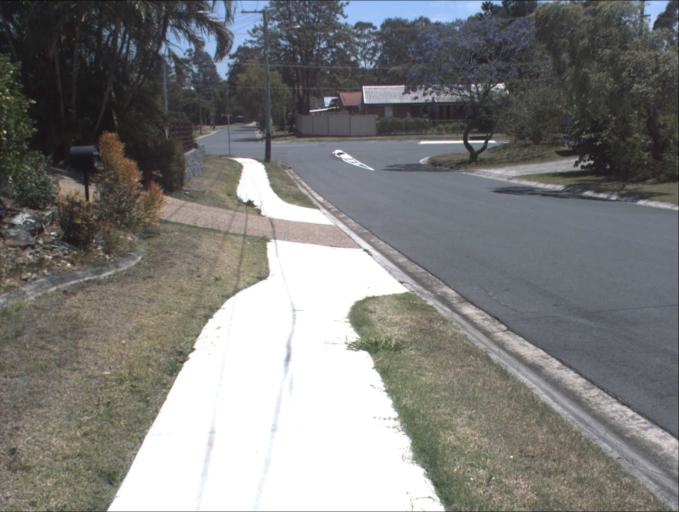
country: AU
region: Queensland
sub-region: Logan
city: Slacks Creek
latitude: -27.6359
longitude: 153.1428
